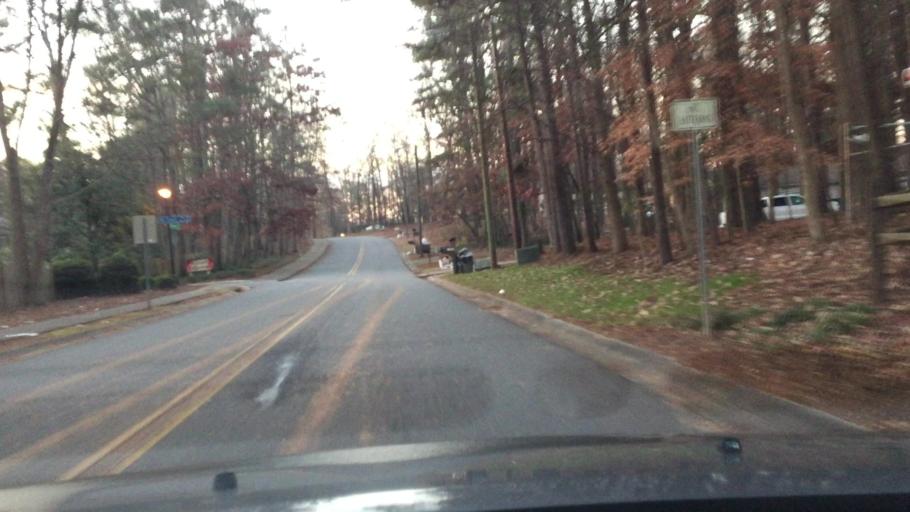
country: US
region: Georgia
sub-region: Cobb County
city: Fair Oaks
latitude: 33.9201
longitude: -84.5744
